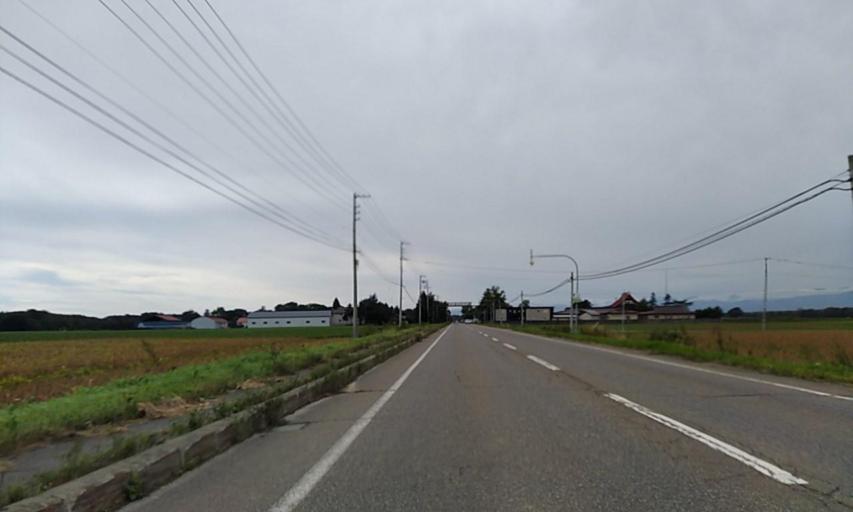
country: JP
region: Hokkaido
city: Obihiro
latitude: 42.8252
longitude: 143.1840
